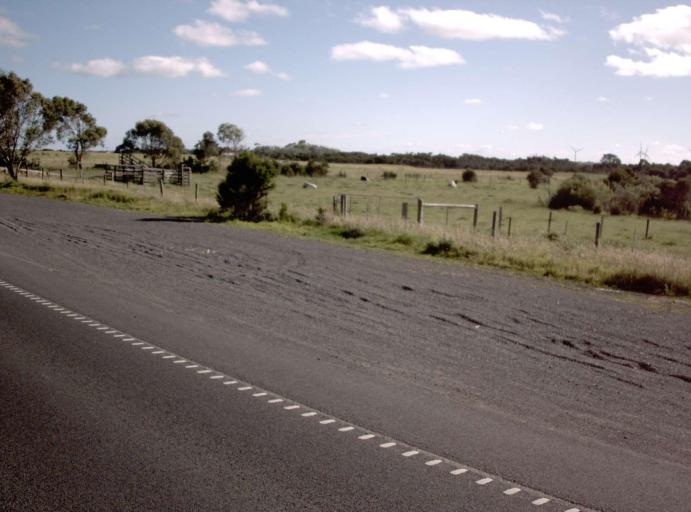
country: AU
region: Victoria
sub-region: Bass Coast
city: North Wonthaggi
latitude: -38.5796
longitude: 145.5742
